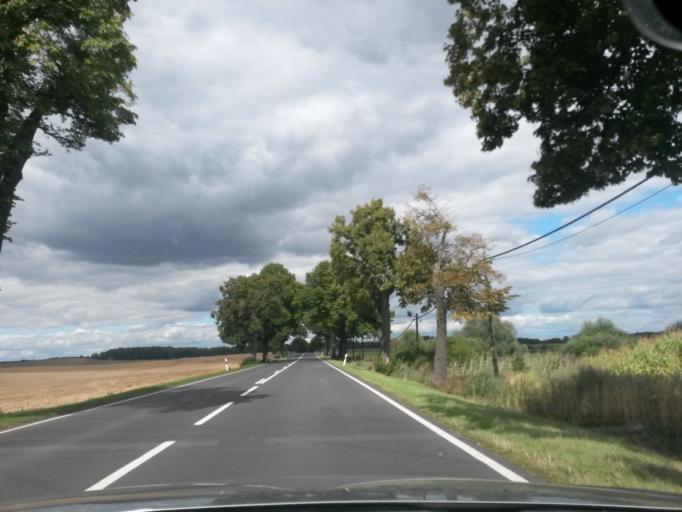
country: DE
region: Brandenburg
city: Angermunde
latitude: 52.9817
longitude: 13.9741
